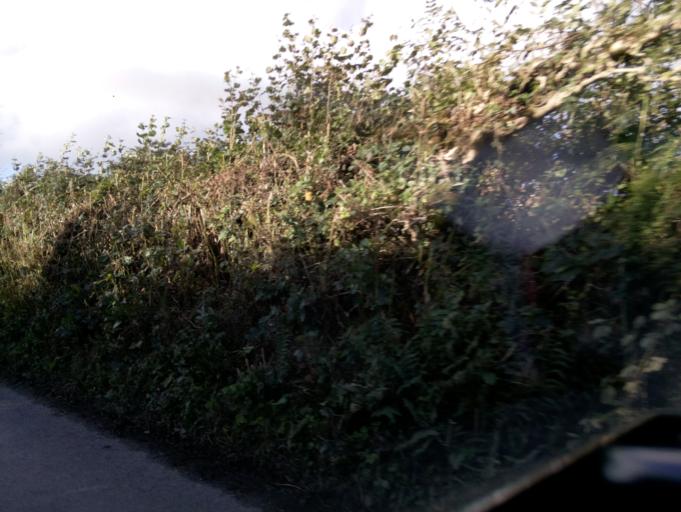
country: GB
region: England
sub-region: Devon
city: Totnes
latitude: 50.3560
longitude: -3.7273
